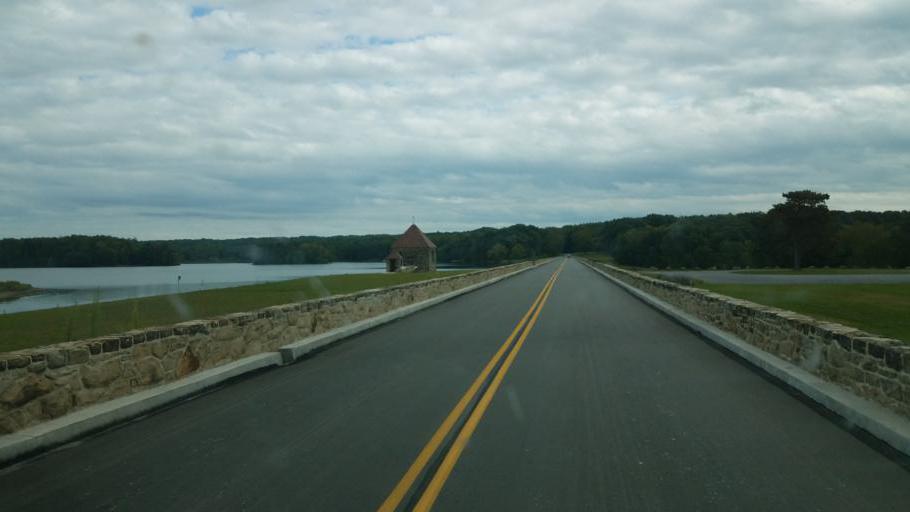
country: US
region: Pennsylvania
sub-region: Crawford County
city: Pymatuning Central
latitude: 41.4972
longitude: -80.4637
